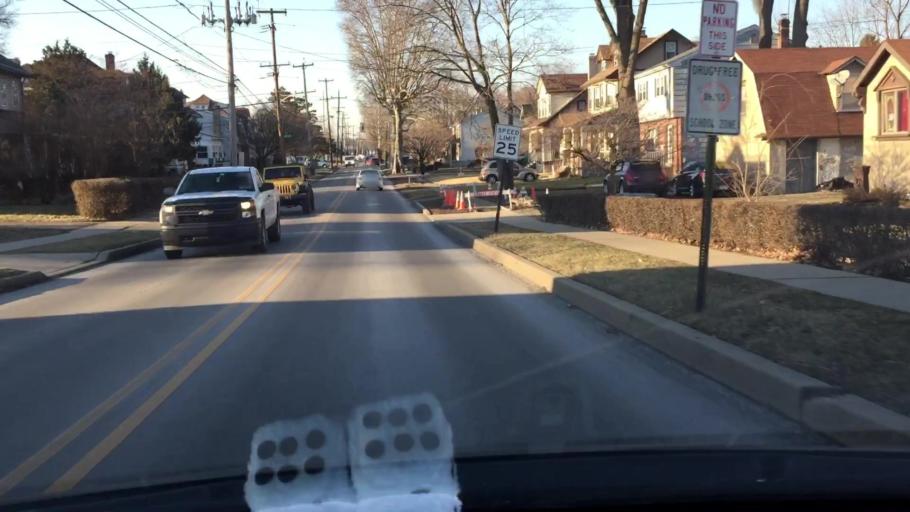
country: US
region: Pennsylvania
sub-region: Delaware County
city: Norwood
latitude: 39.8916
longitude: -75.3030
